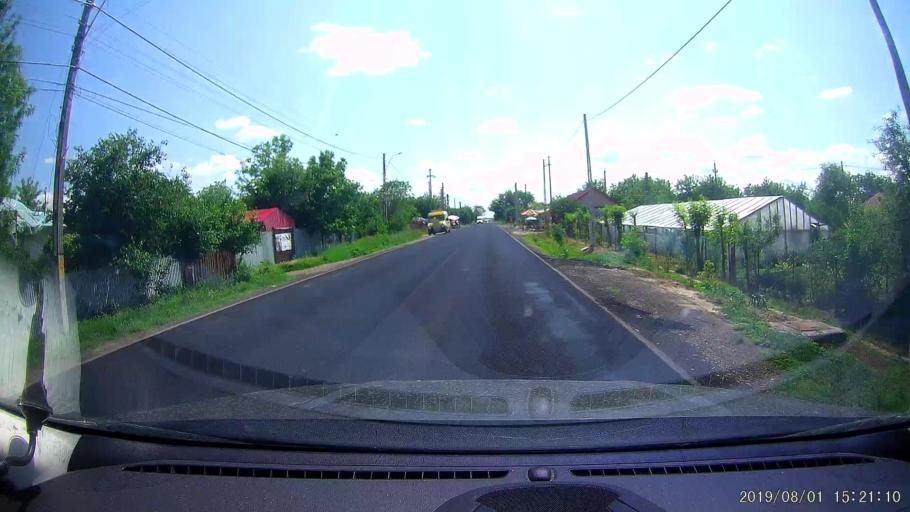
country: RO
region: Braila
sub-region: Comuna Tufesti
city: Tufesti
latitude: 45.0727
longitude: 27.7995
